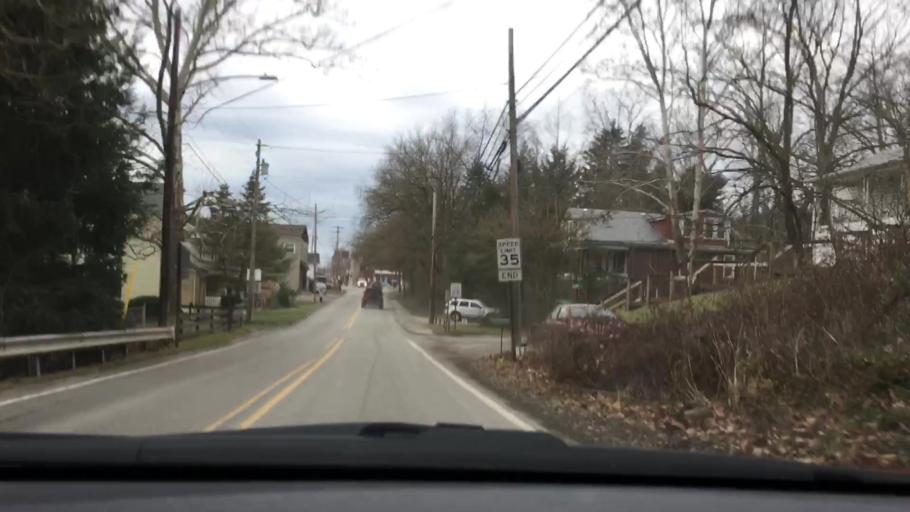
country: US
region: Pennsylvania
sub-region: Washington County
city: McDonald
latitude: 40.3723
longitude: -80.2271
